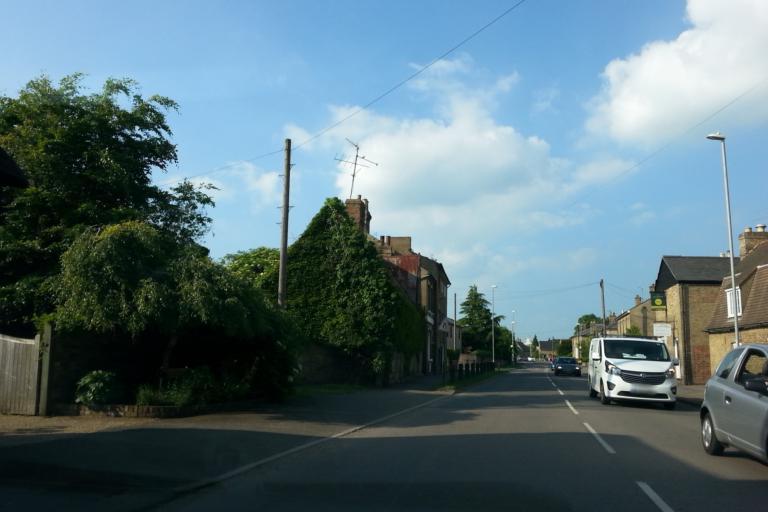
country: GB
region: England
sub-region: Cambridgeshire
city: Earith
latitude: 52.3112
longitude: 0.0554
